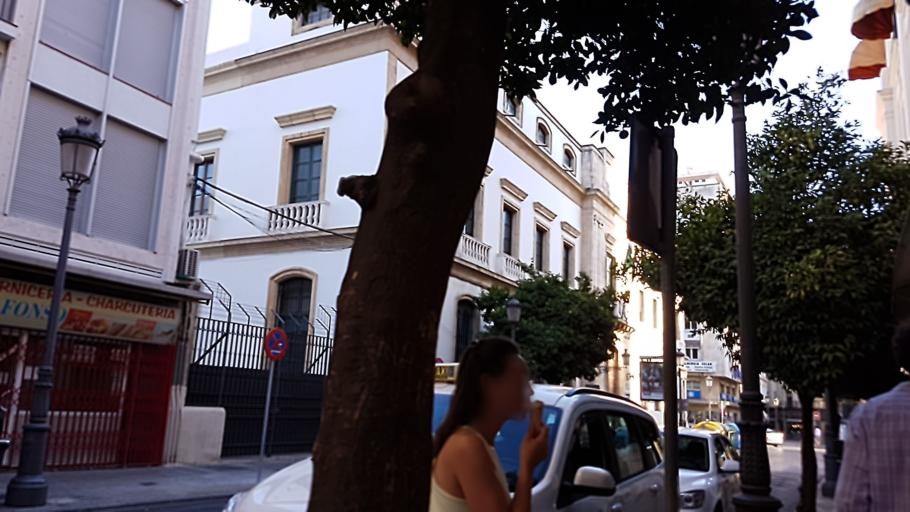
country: ES
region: Andalusia
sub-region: Province of Cordoba
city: Cordoba
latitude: 37.8851
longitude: -4.7793
